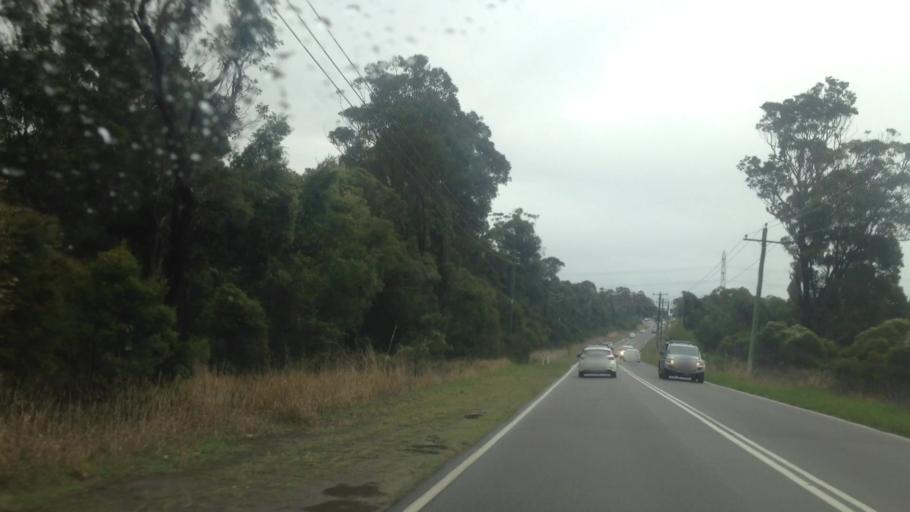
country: AU
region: New South Wales
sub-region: Wyong Shire
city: Charmhaven
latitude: -33.1624
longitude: 151.4784
